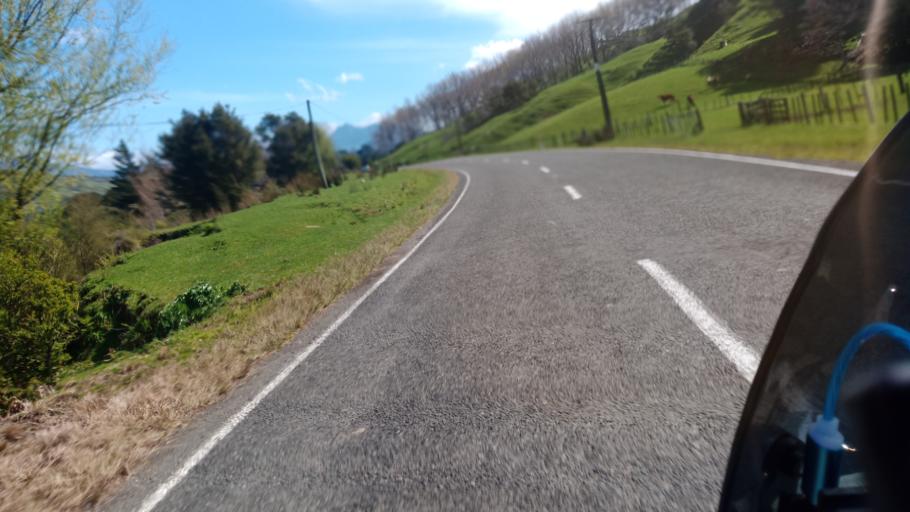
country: NZ
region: Gisborne
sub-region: Gisborne District
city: Gisborne
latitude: -37.8641
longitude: 178.2331
